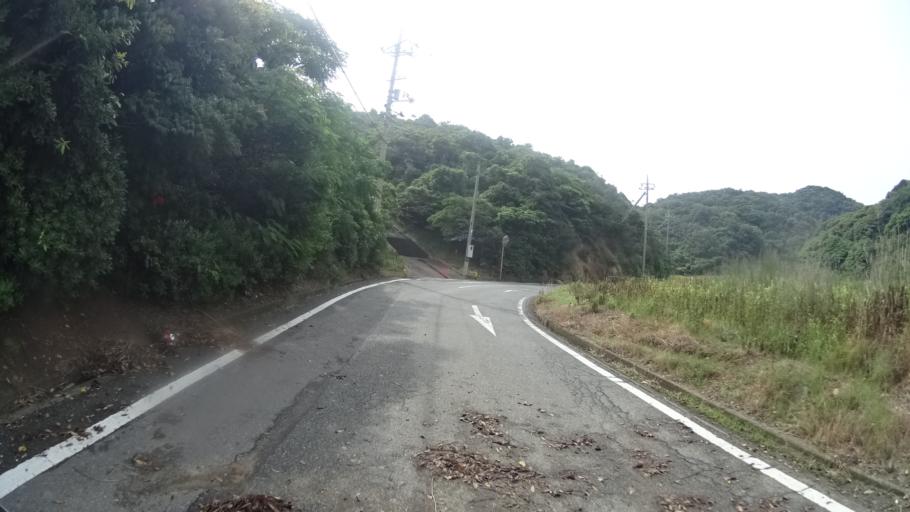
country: JP
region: Yamaguchi
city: Shimonoseki
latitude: 34.0974
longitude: 130.8754
